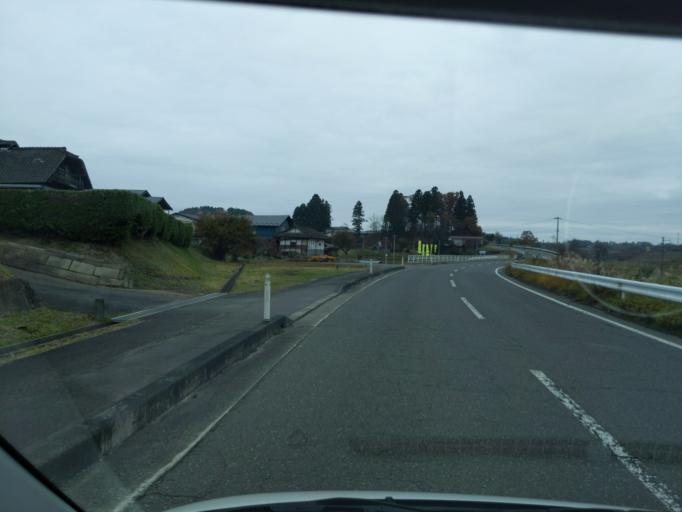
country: JP
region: Iwate
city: Mizusawa
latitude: 39.1966
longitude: 141.2216
